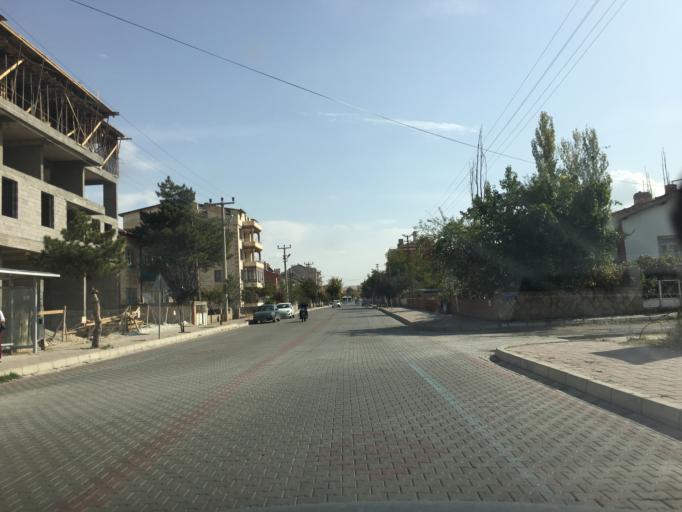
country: TR
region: Nevsehir
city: Avanos
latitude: 38.7118
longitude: 34.8458
